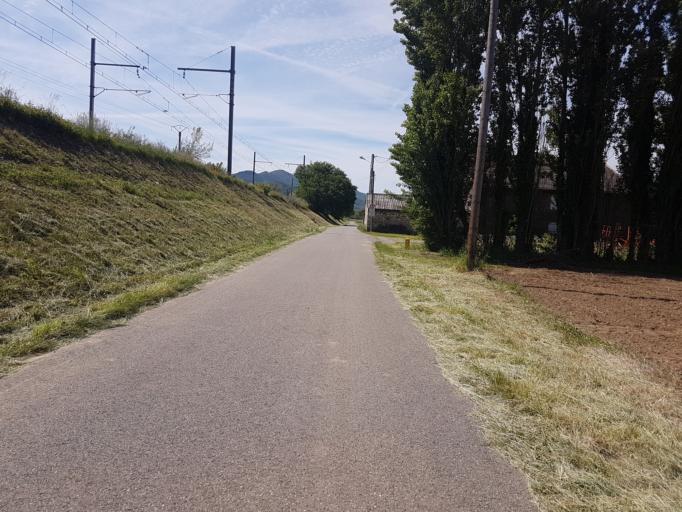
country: FR
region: Rhone-Alpes
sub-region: Departement de l'Ardeche
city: Le Pouzin
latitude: 44.7371
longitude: 4.7475
